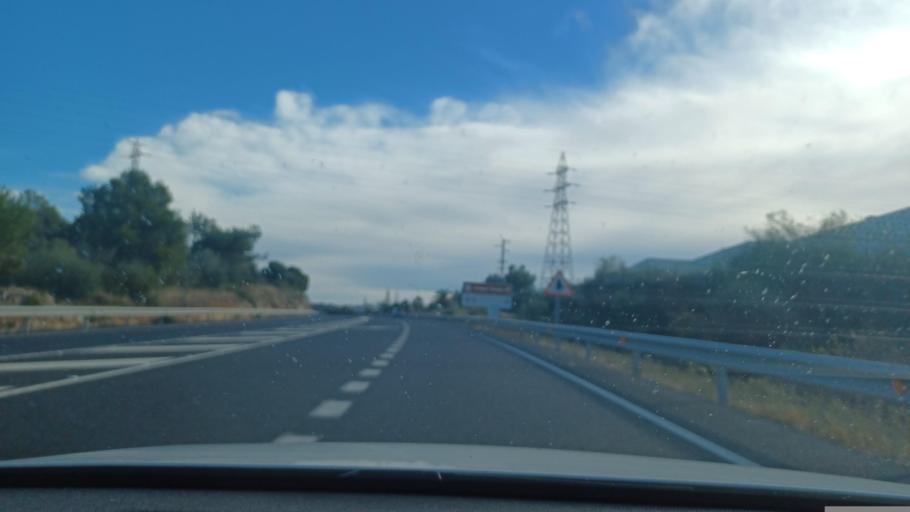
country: ES
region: Catalonia
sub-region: Provincia de Tarragona
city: El Perello
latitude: 40.8700
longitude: 0.7156
